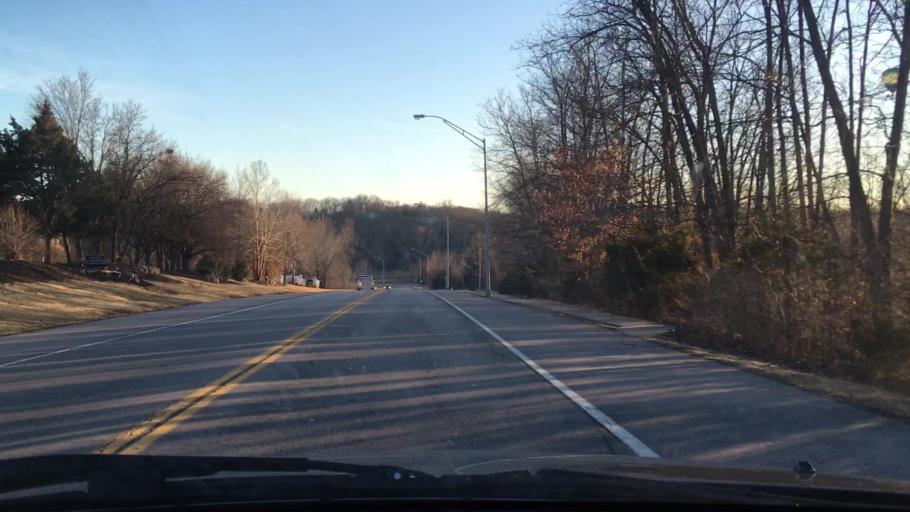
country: US
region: Missouri
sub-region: Boone County
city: Columbia
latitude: 38.9258
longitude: -92.3647
